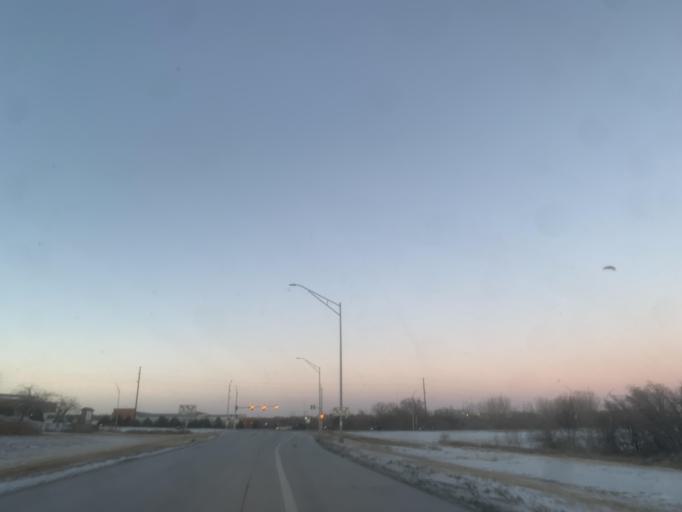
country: US
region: Nebraska
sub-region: Douglas County
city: Ralston
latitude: 41.2039
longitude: -96.0966
